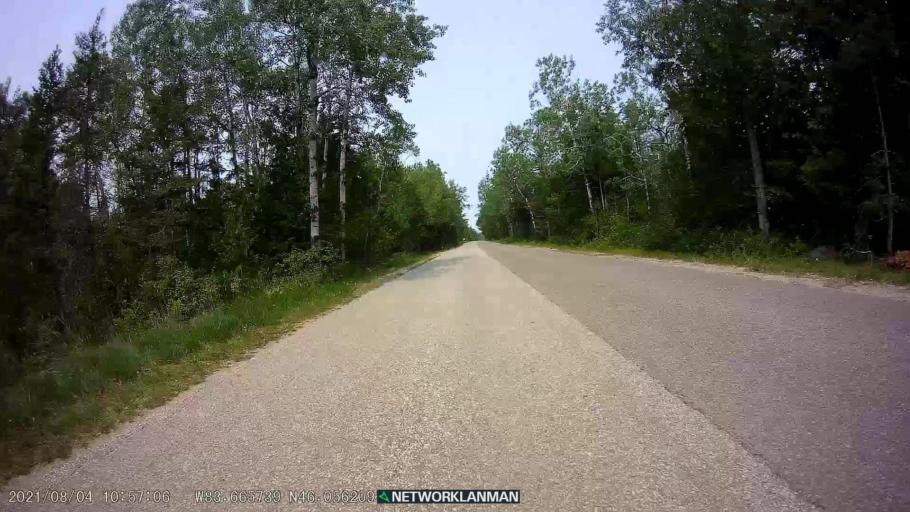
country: CA
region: Ontario
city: Thessalon
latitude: 46.0551
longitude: -83.6657
